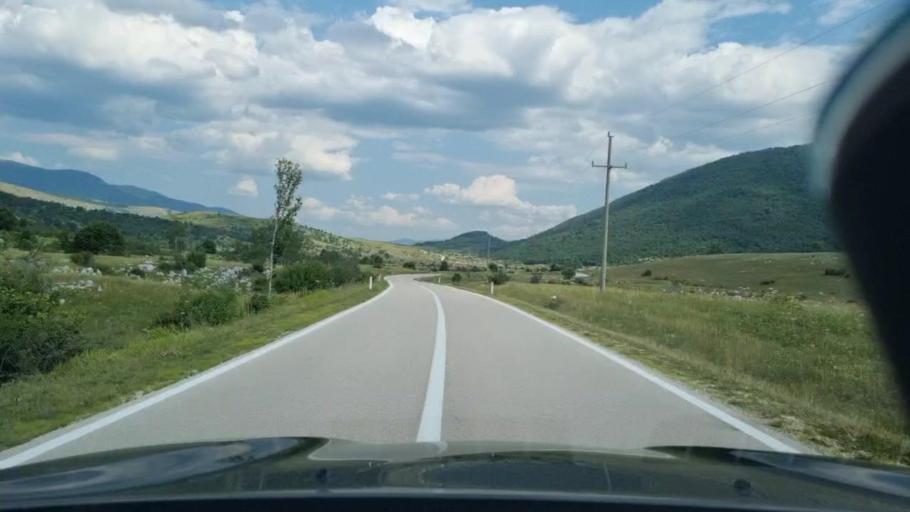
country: BA
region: Federation of Bosnia and Herzegovina
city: Bosansko Grahovo
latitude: 44.1398
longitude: 16.4702
